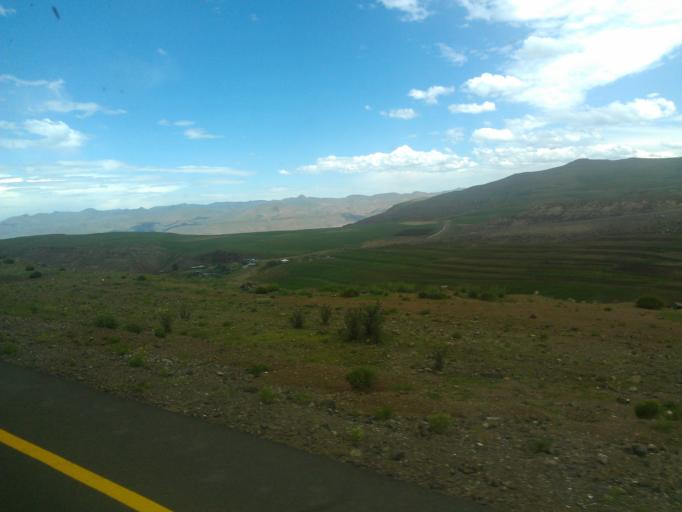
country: LS
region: Maseru
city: Nako
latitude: -29.9877
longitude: 28.1491
